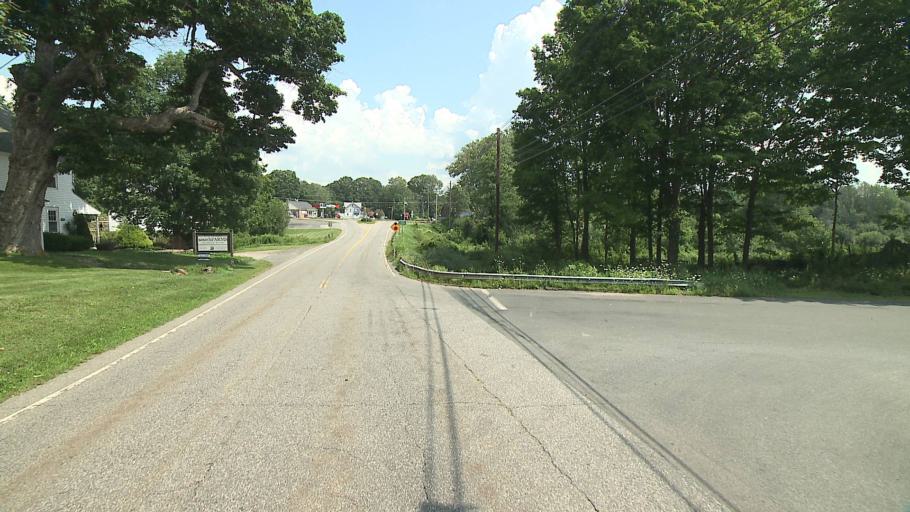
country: US
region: Connecticut
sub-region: Litchfield County
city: Bethlehem Village
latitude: 41.6882
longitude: -73.1822
